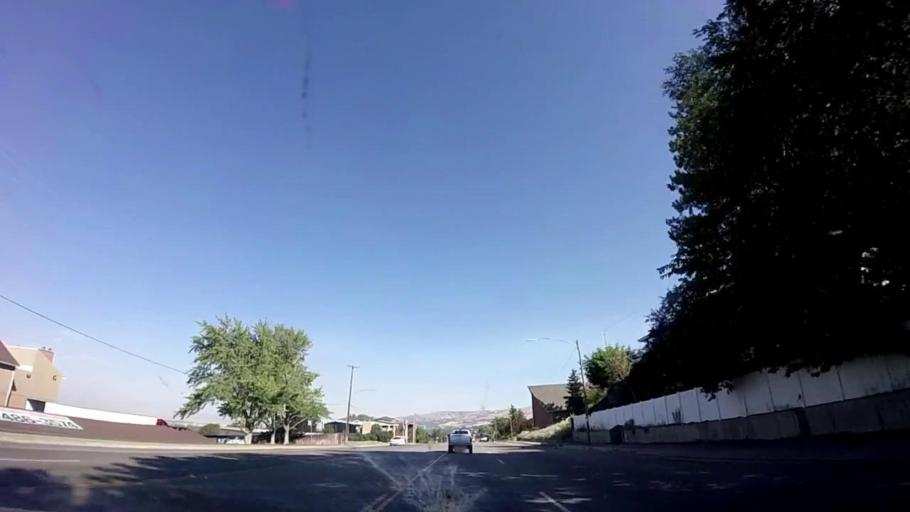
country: US
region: Utah
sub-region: Salt Lake County
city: Canyon Rim
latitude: 40.7234
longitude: -111.8131
